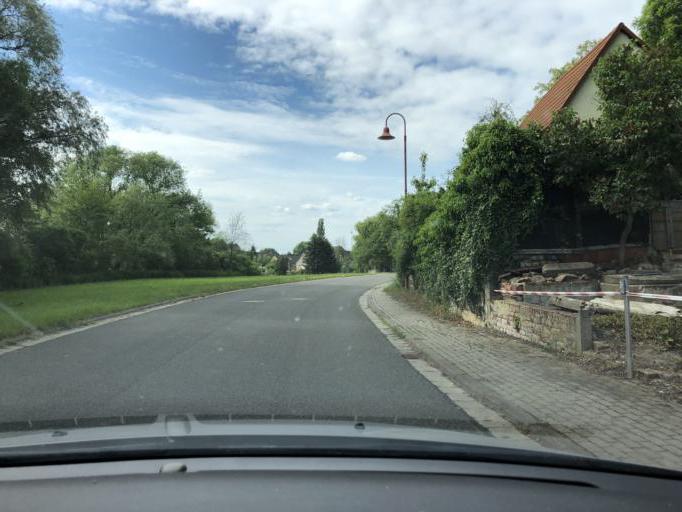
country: DE
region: Saxony
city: Nerchau
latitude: 51.2138
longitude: 12.8144
